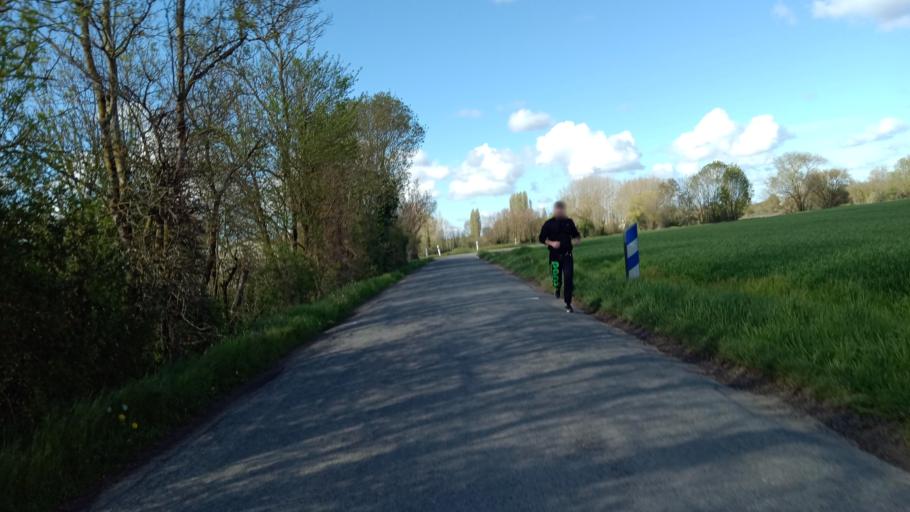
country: FR
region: Poitou-Charentes
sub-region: Departement de la Charente-Maritime
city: Verines
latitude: 46.1491
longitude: -0.9363
